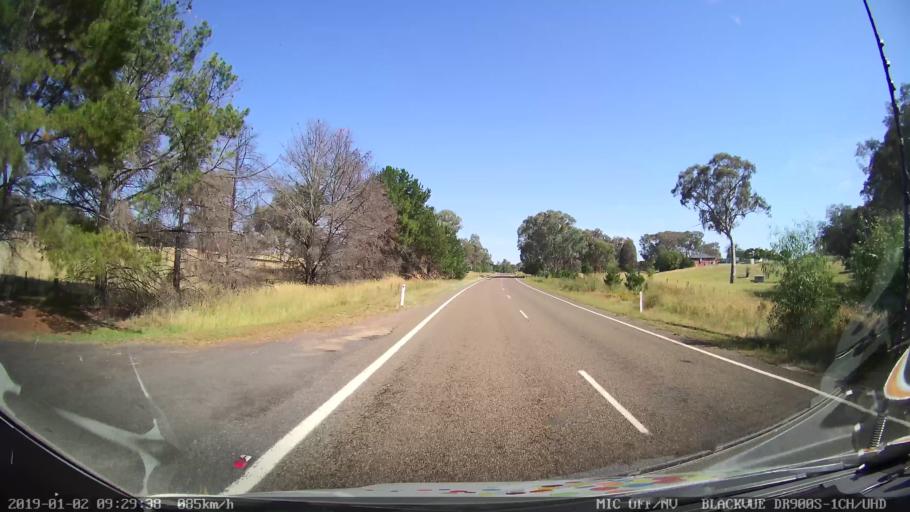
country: AU
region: New South Wales
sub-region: Tumut Shire
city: Tumut
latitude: -35.3364
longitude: 148.2406
